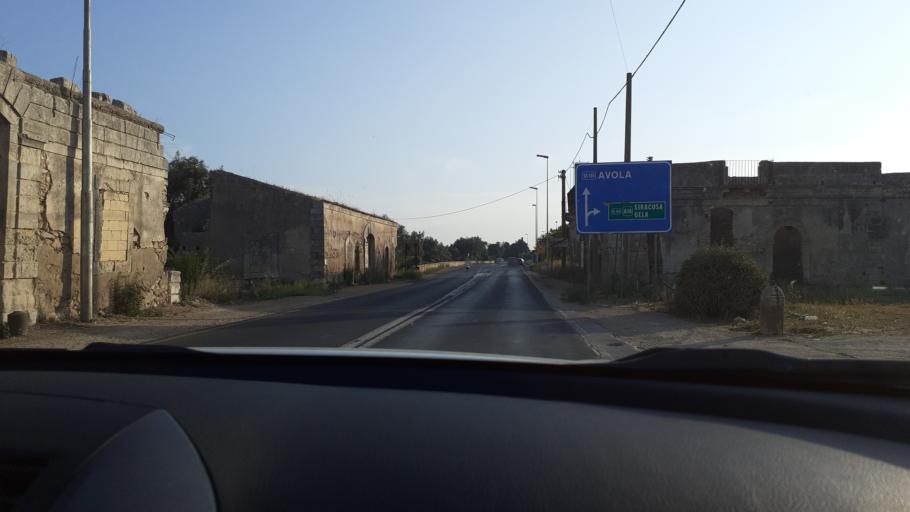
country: IT
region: Sicily
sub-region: Provincia di Siracusa
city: Cassibile
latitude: 36.9729
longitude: 15.1931
